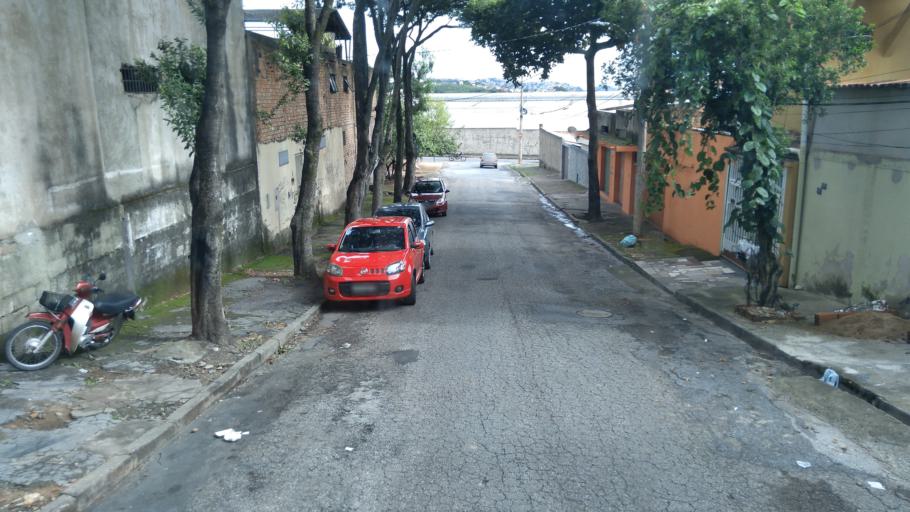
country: BR
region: Minas Gerais
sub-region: Belo Horizonte
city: Belo Horizonte
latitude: -19.8686
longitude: -43.9034
